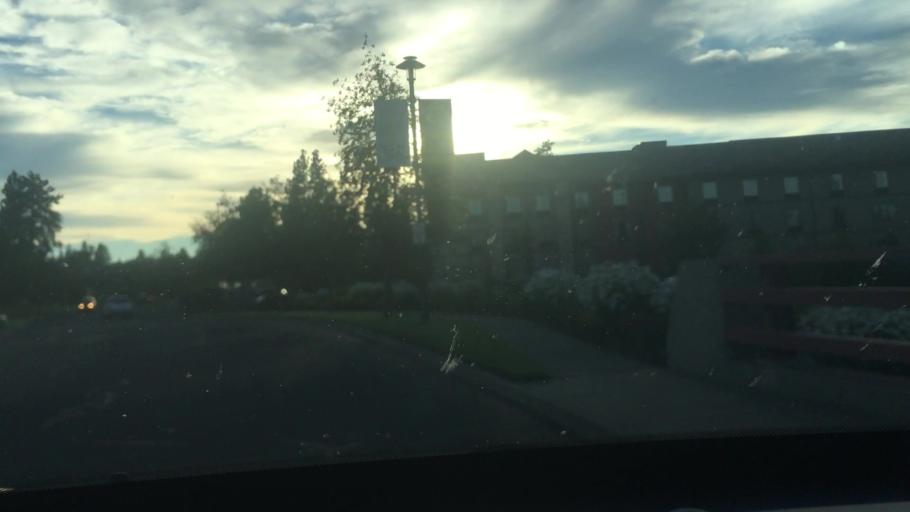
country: US
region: Oregon
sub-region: Deschutes County
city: Bend
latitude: 44.0436
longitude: -121.3174
